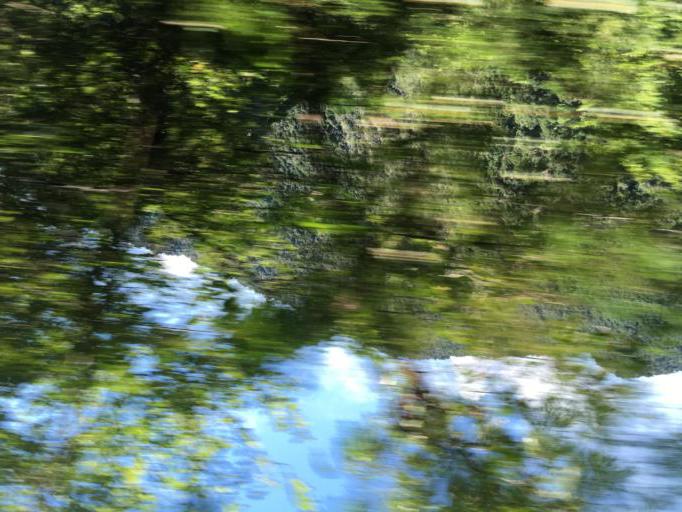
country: TW
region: Taiwan
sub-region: Yilan
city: Yilan
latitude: 24.4186
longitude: 121.7351
